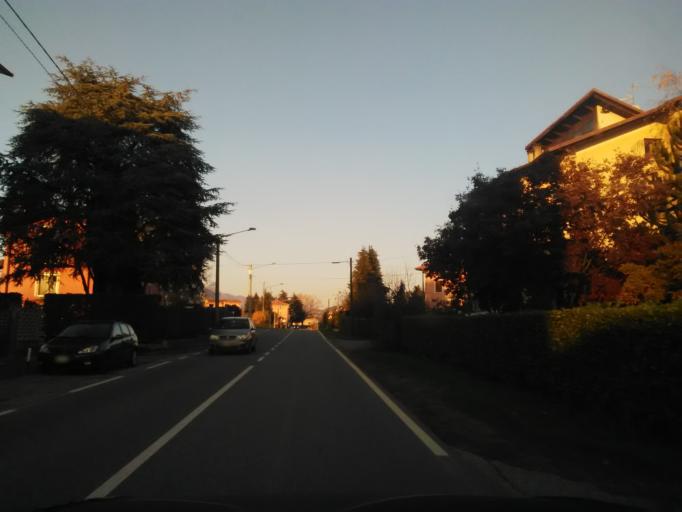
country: IT
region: Piedmont
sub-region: Provincia di Biella
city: Ponderano
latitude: 45.5330
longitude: 8.0474
